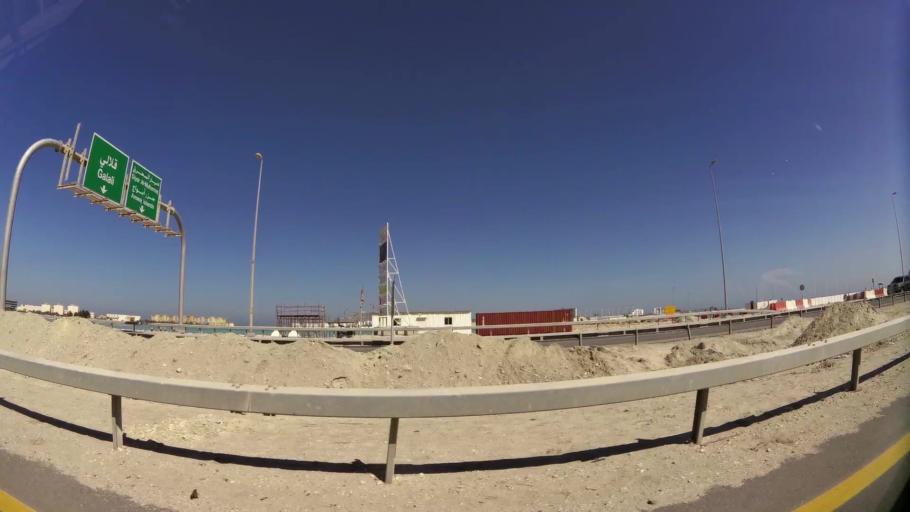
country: BH
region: Muharraq
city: Al Hadd
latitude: 26.2708
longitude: 50.6617
